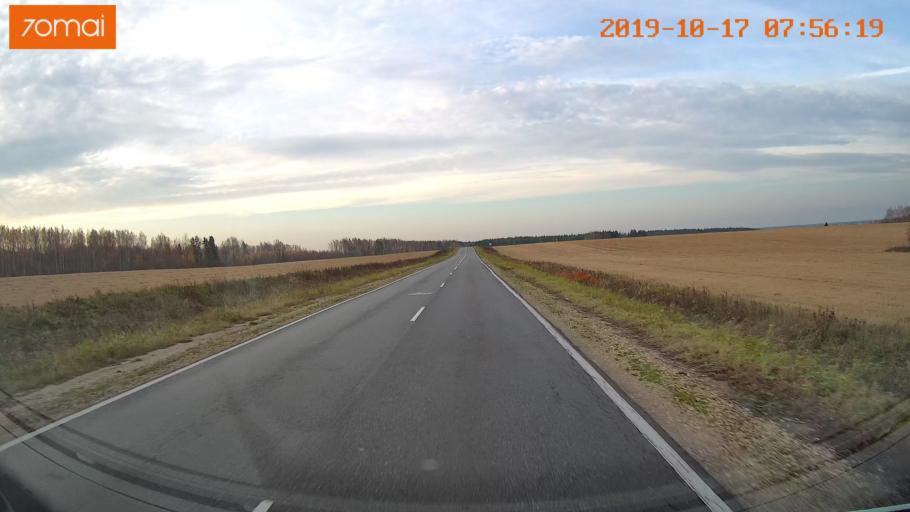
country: RU
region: Vladimir
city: Bavleny
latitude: 56.4246
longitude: 39.5919
